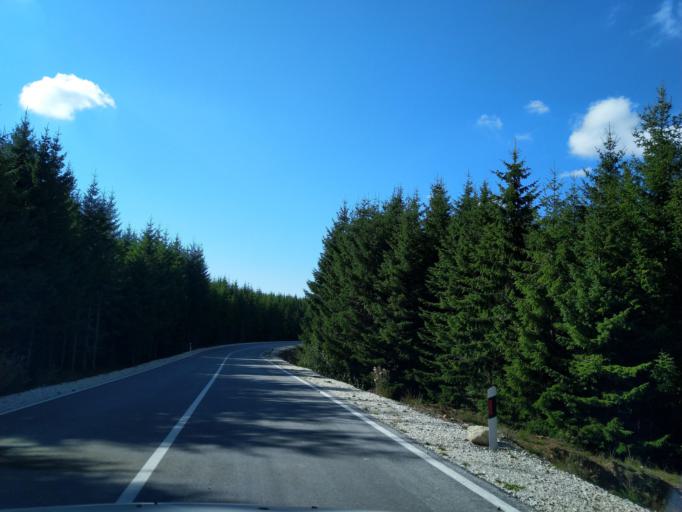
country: RS
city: Sokolovica
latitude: 43.2903
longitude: 20.3134
